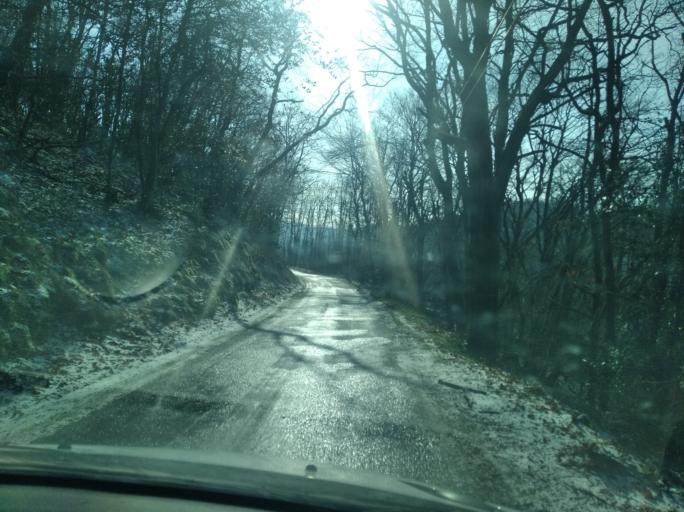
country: FR
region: Auvergne
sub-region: Departement de l'Allier
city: Le Mayet-de-Montagne
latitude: 46.1726
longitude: 3.7381
